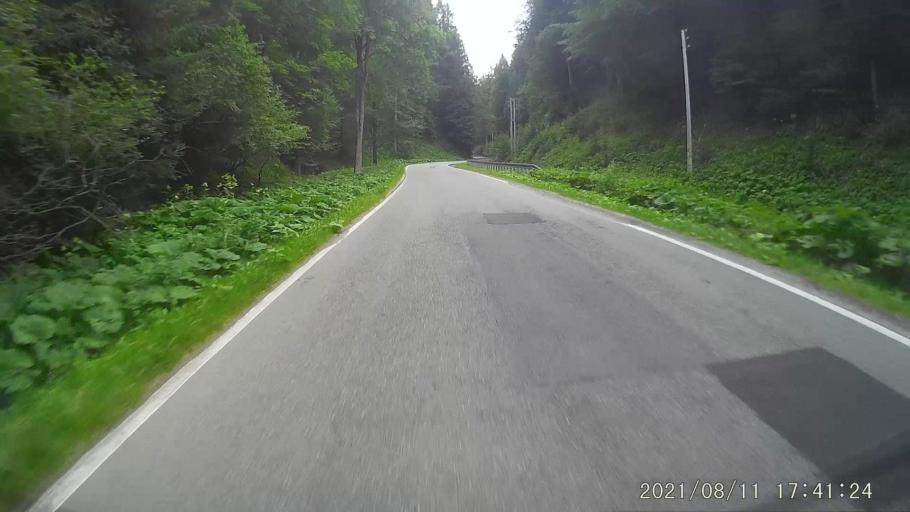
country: PL
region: Lower Silesian Voivodeship
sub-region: Powiat klodzki
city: Duszniki-Zdroj
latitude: 50.3668
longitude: 16.3919
